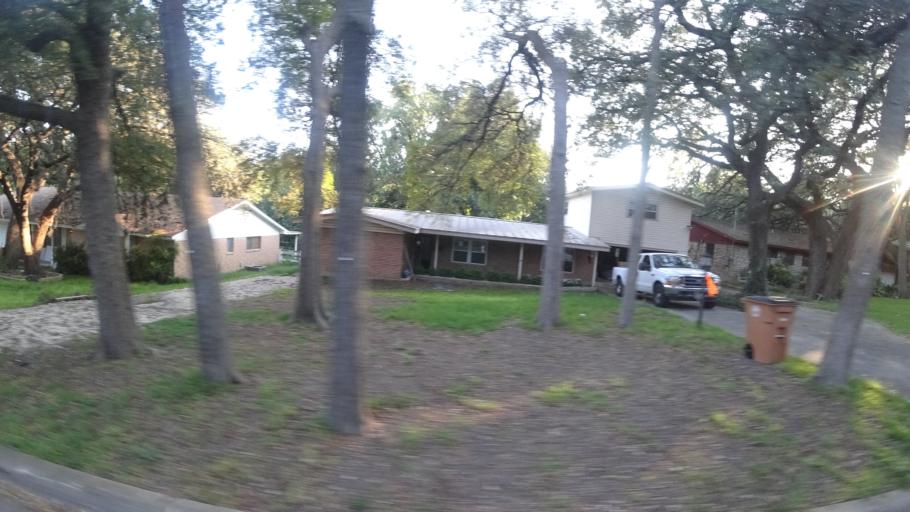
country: US
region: Texas
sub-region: Travis County
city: Wells Branch
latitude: 30.3664
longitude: -97.6735
